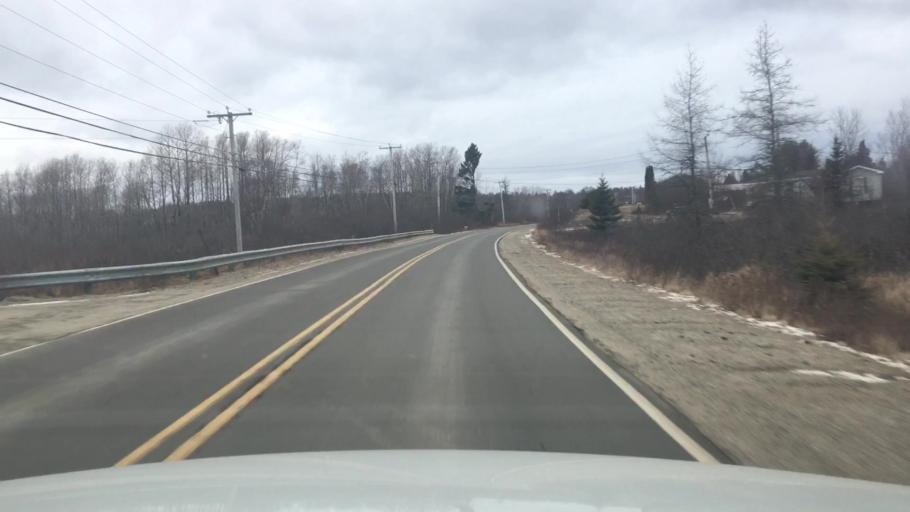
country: US
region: Maine
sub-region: Washington County
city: Jonesport
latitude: 44.5528
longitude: -67.6242
